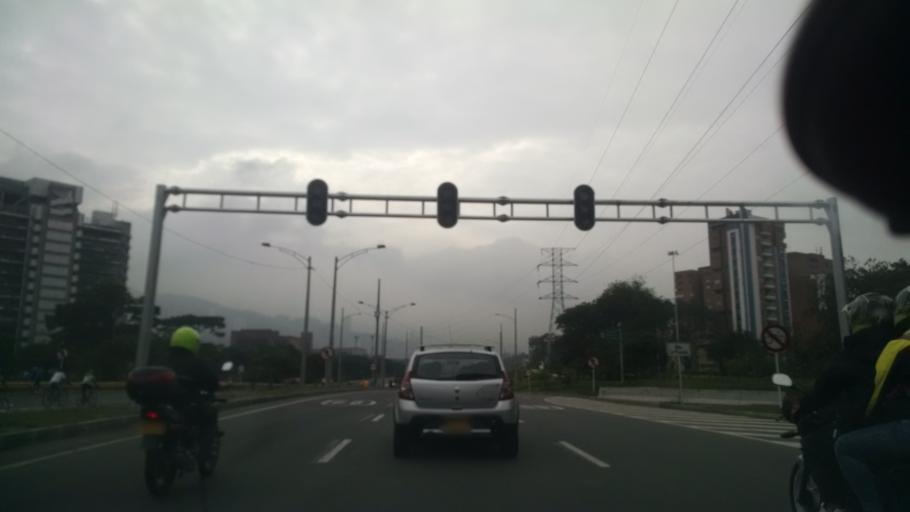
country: CO
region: Antioquia
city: Medellin
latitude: 6.2469
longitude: -75.5805
